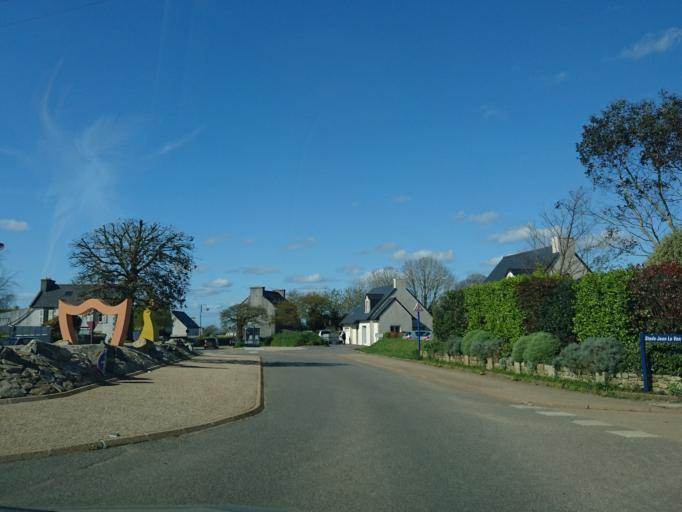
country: FR
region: Brittany
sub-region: Departement du Finistere
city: Lanrivoare
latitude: 48.4707
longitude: -4.6393
